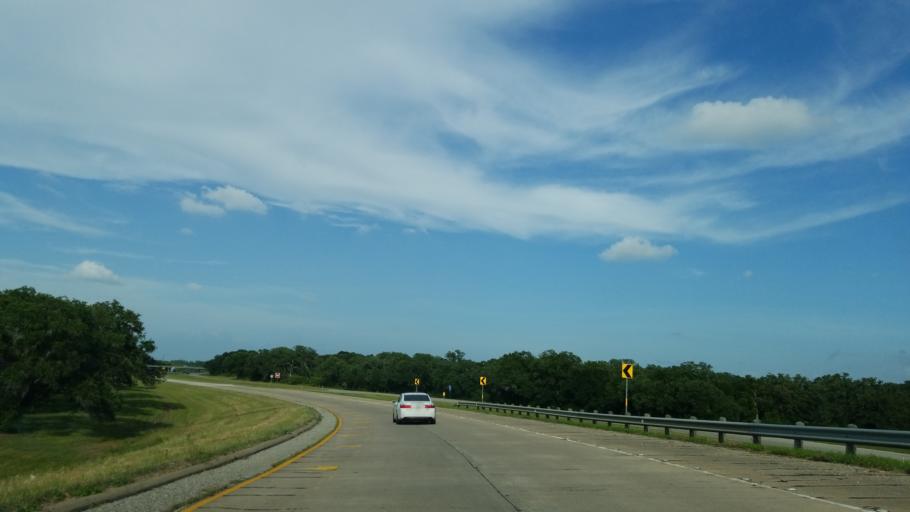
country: US
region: Texas
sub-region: Colorado County
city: Columbus
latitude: 29.6925
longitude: -96.5714
